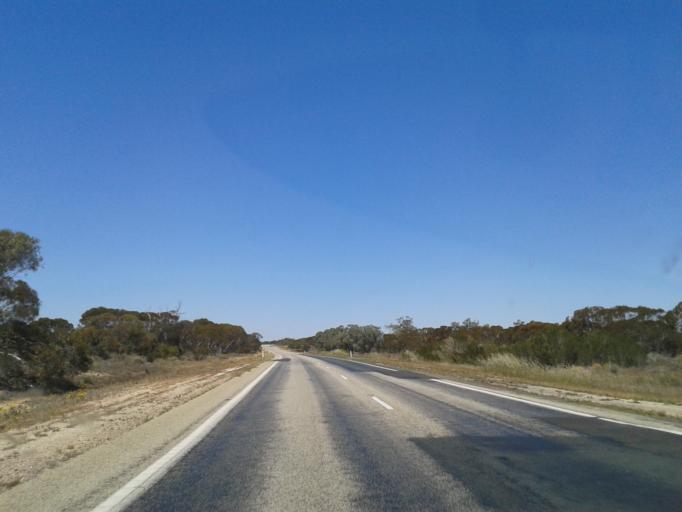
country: AU
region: New South Wales
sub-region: Wentworth
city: Gol Gol
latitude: -34.4127
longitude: 142.4411
